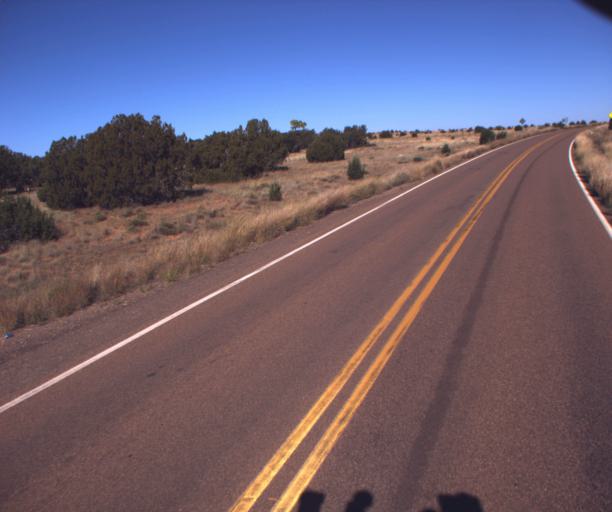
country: US
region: Arizona
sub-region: Navajo County
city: Heber-Overgaard
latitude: 34.4816
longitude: -110.3391
